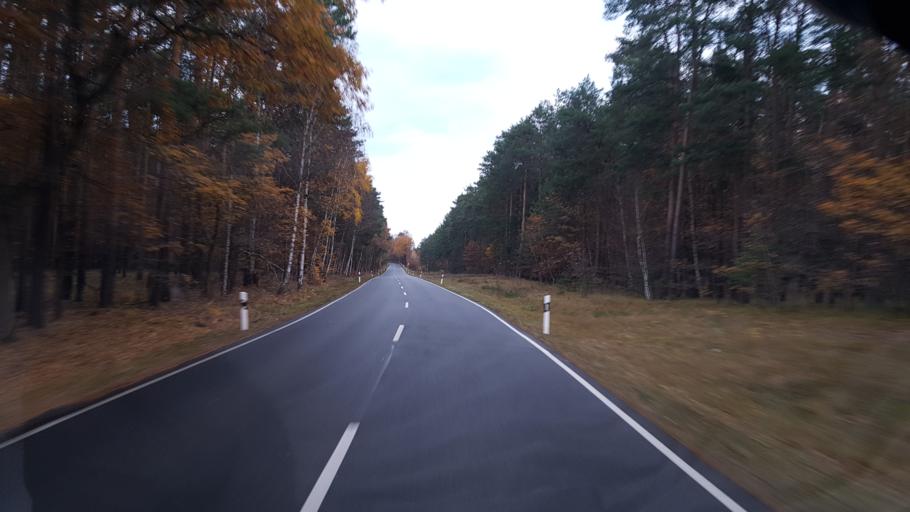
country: DE
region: Brandenburg
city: Ortrand
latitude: 51.3909
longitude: 13.7649
